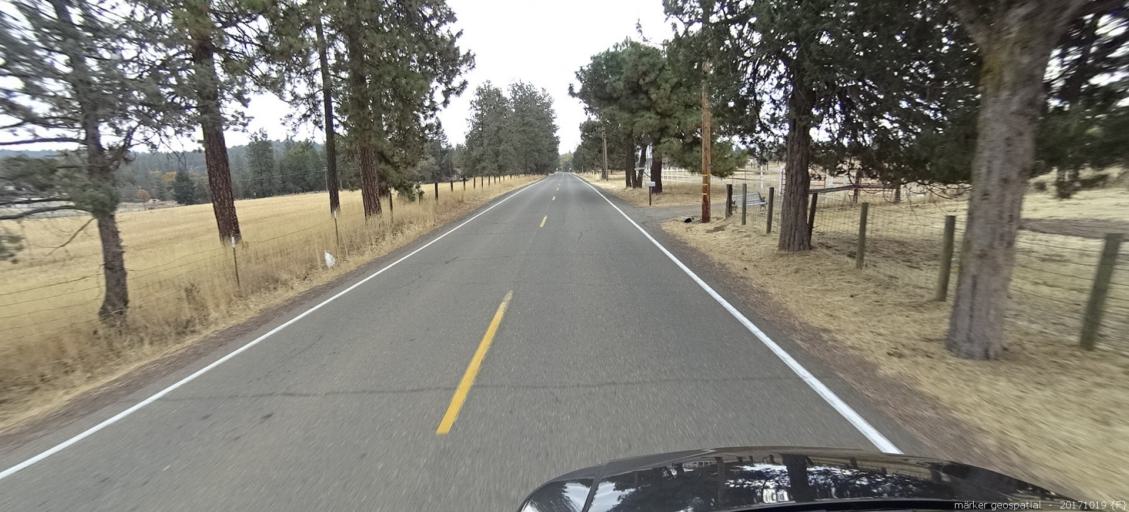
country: US
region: California
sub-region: Shasta County
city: Burney
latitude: 41.0505
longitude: -121.3436
